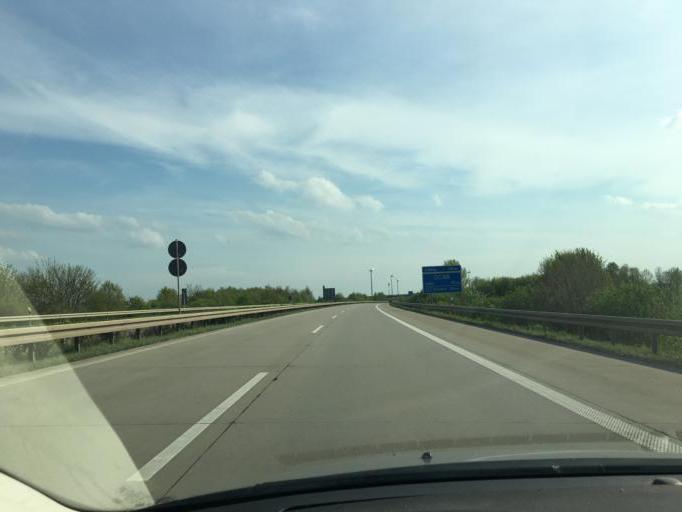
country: DE
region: Saxony-Anhalt
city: Dahlenwarsleben
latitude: 52.1959
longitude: 11.5509
